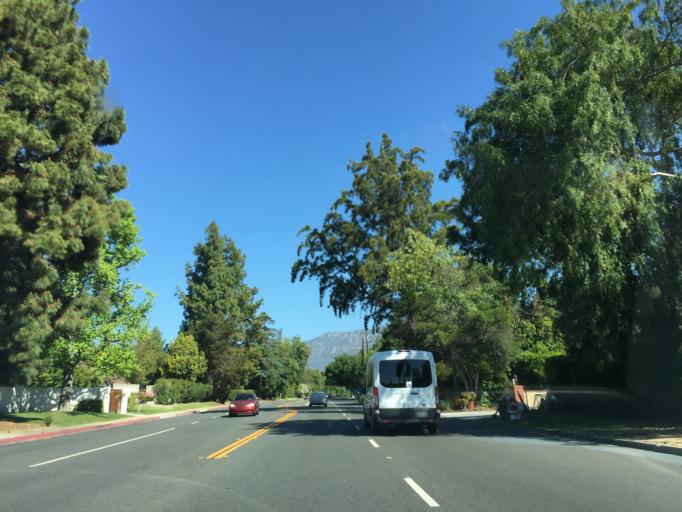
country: US
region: California
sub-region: Los Angeles County
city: East Pasadena
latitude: 34.1326
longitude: -118.0935
